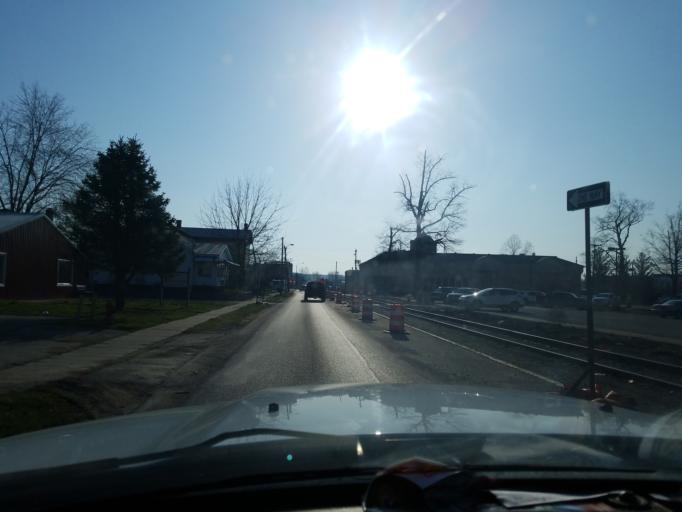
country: US
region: Indiana
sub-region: Owen County
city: Spencer
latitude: 39.2861
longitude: -86.7649
